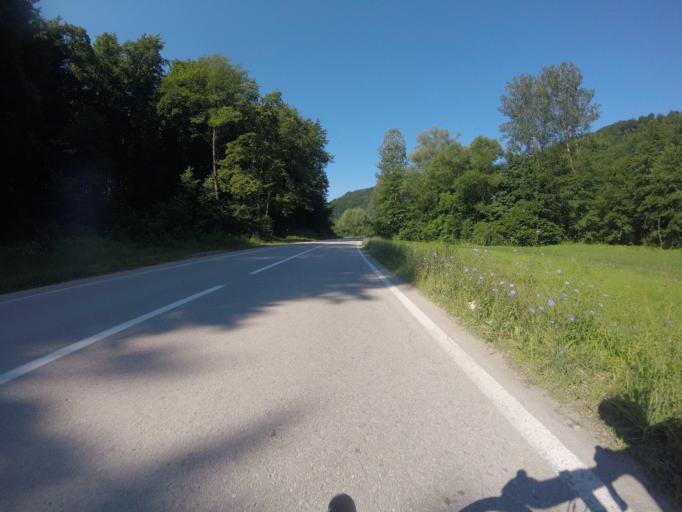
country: HR
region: Zagrebacka
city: Bregana
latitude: 45.8351
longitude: 15.6577
